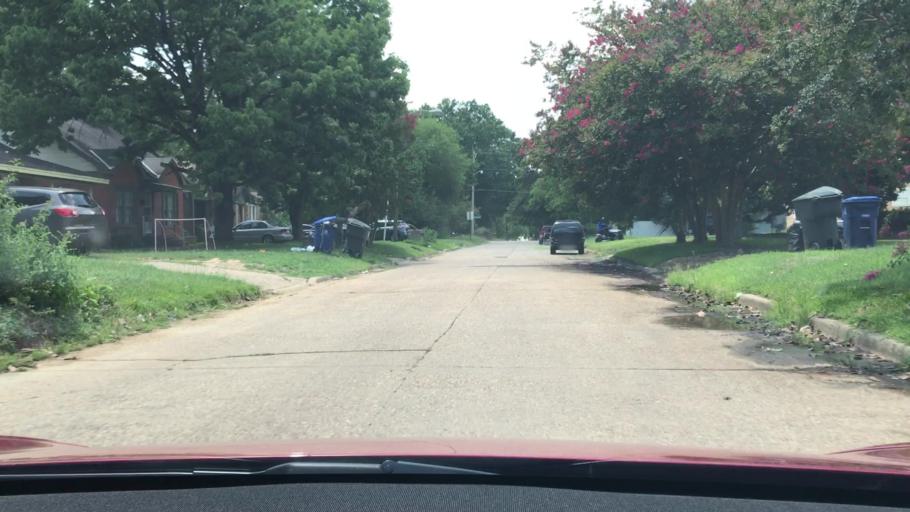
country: US
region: Louisiana
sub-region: Bossier Parish
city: Bossier City
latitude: 32.4963
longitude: -93.7278
